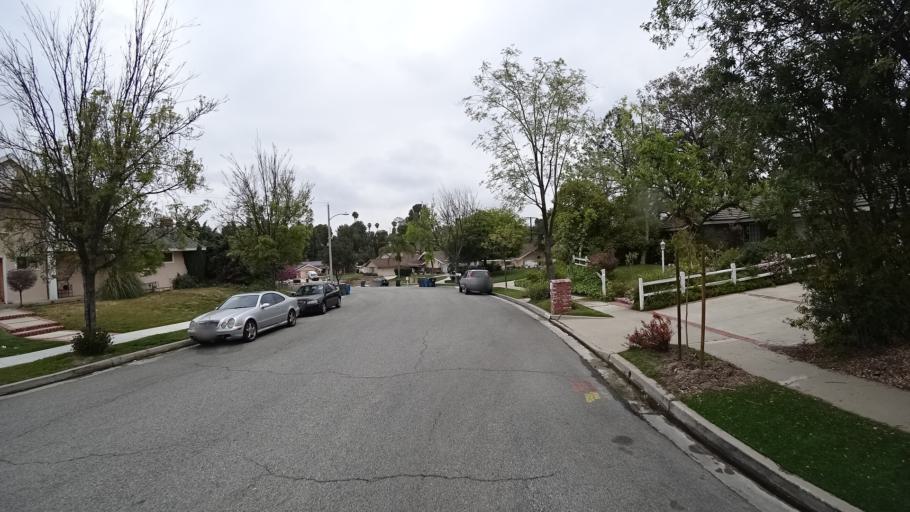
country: US
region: California
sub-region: Ventura County
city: Thousand Oaks
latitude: 34.2052
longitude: -118.8750
